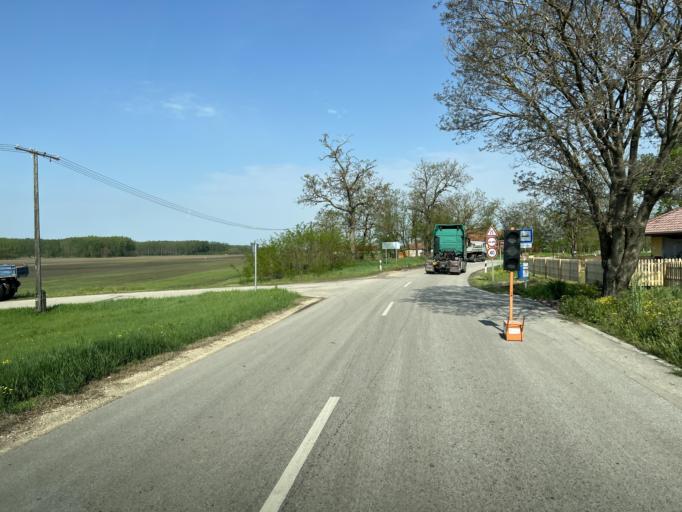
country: HU
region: Pest
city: Kocser
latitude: 46.9824
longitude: 19.9831
